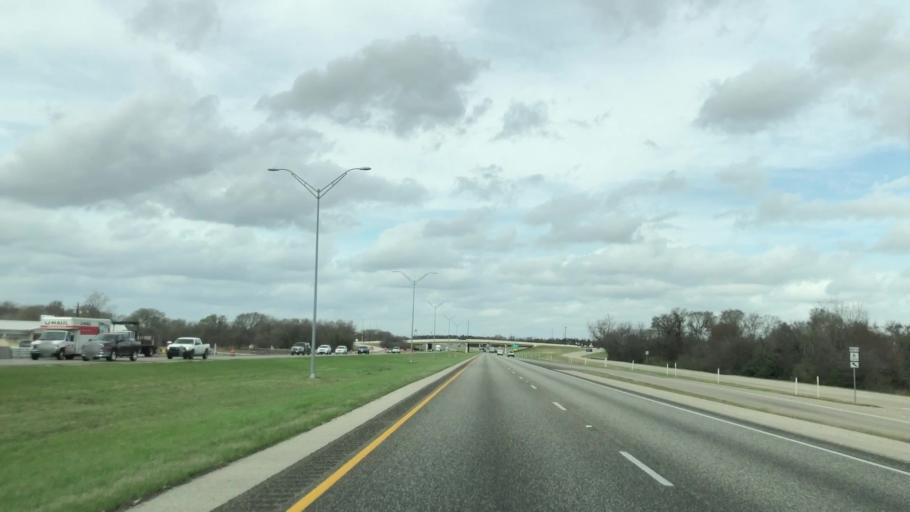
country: US
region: Texas
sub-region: Brazos County
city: Bryan
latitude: 30.6833
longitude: -96.3461
